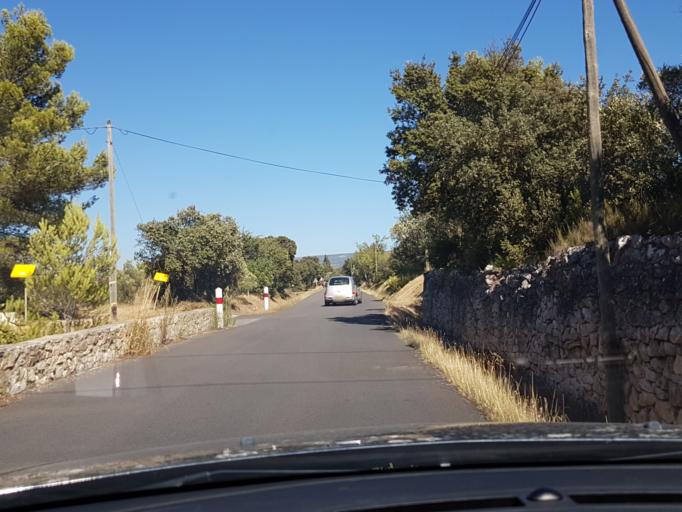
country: FR
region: Provence-Alpes-Cote d'Azur
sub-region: Departement des Bouches-du-Rhone
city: Orgon
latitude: 43.7835
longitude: 5.0161
